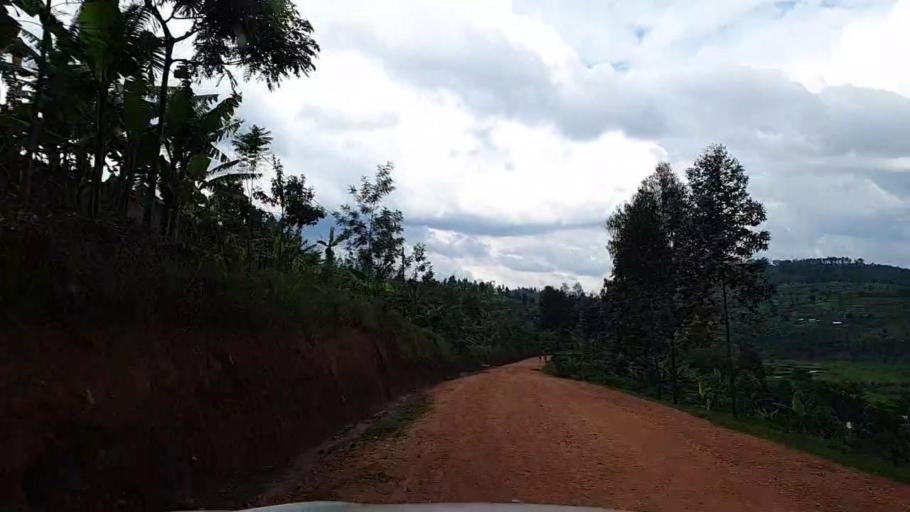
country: RW
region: Southern Province
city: Nyanza
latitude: -2.4138
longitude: 29.6712
